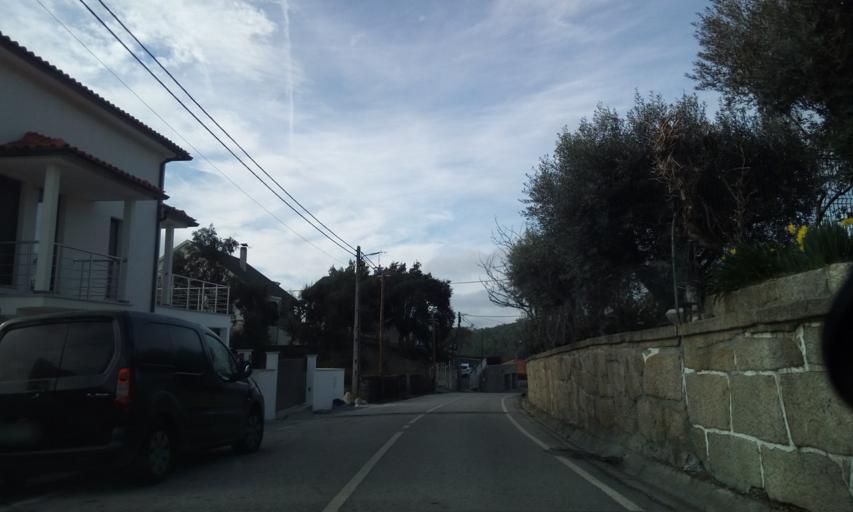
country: PT
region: Guarda
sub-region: Aguiar da Beira
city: Aguiar da Beira
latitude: 40.7297
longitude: -7.5568
